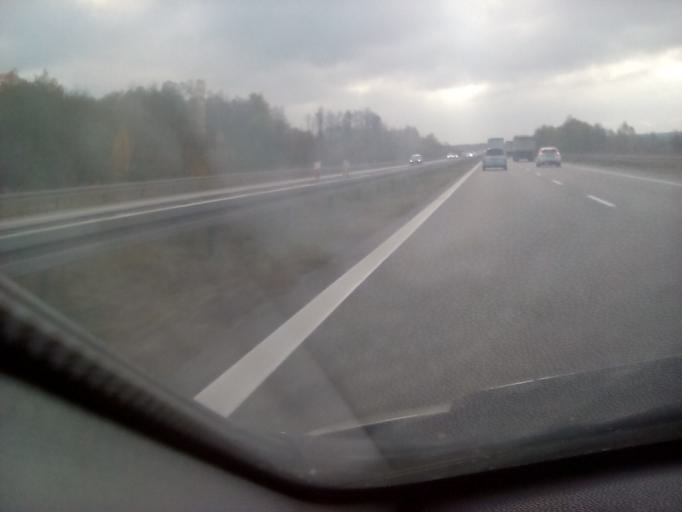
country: PL
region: Masovian Voivodeship
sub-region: Powiat bialobrzeski
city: Promna
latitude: 51.6700
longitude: 20.9506
